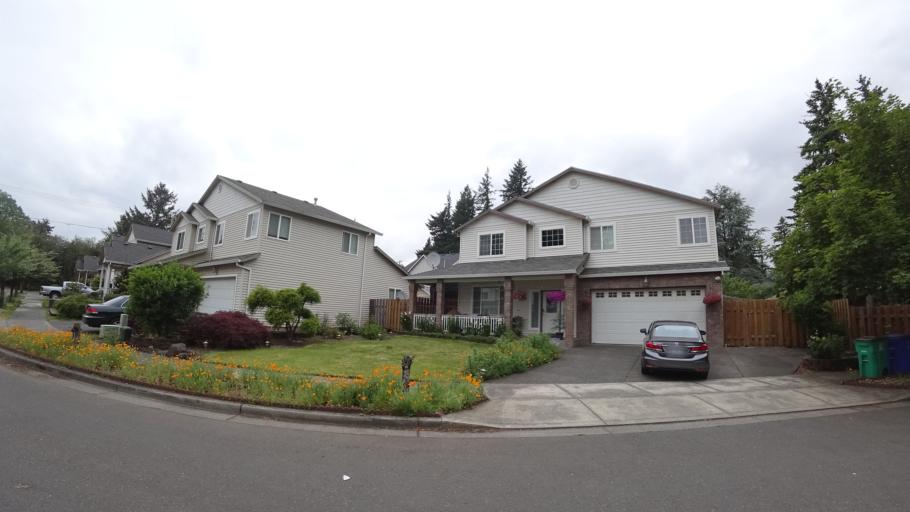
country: US
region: Oregon
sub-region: Multnomah County
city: Lents
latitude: 45.5073
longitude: -122.5202
